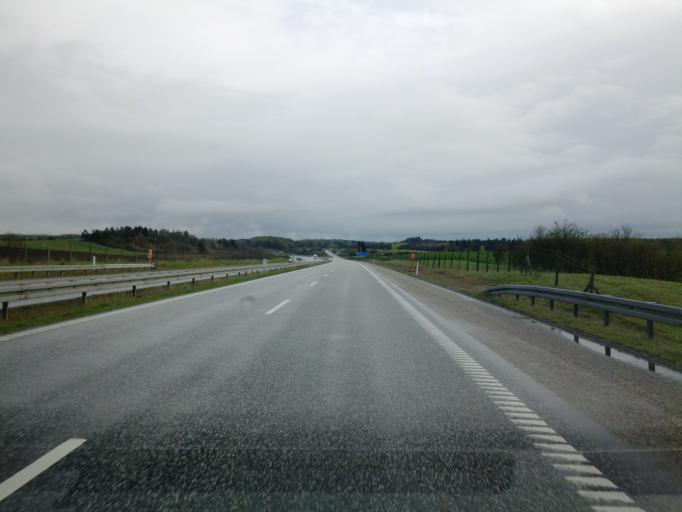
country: DK
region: North Denmark
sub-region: Bronderslev Kommune
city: Hjallerup
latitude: 57.2046
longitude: 10.2086
